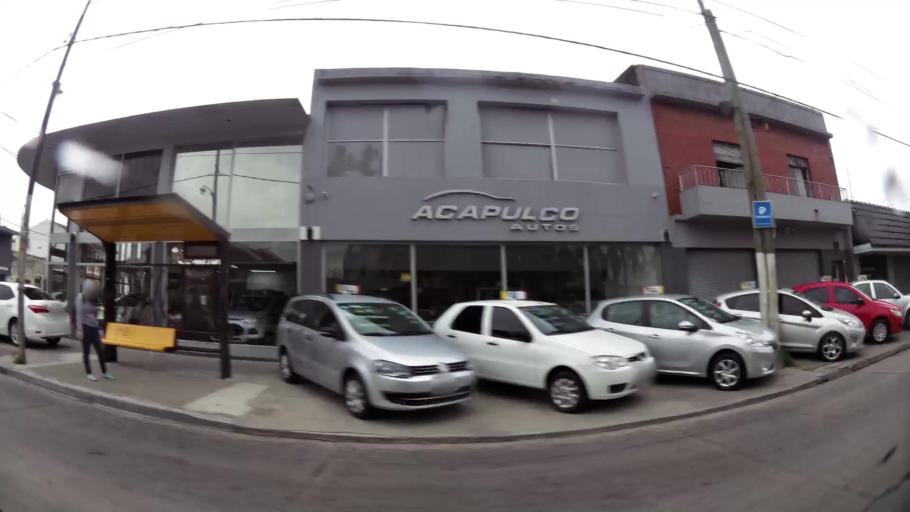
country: AR
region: Buenos Aires
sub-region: Partido de Lanus
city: Lanus
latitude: -34.6828
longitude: -58.4016
